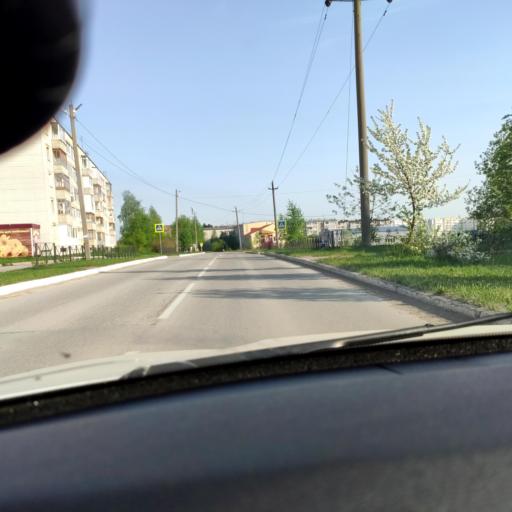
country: RU
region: Perm
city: Polazna
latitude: 58.2946
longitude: 56.3929
